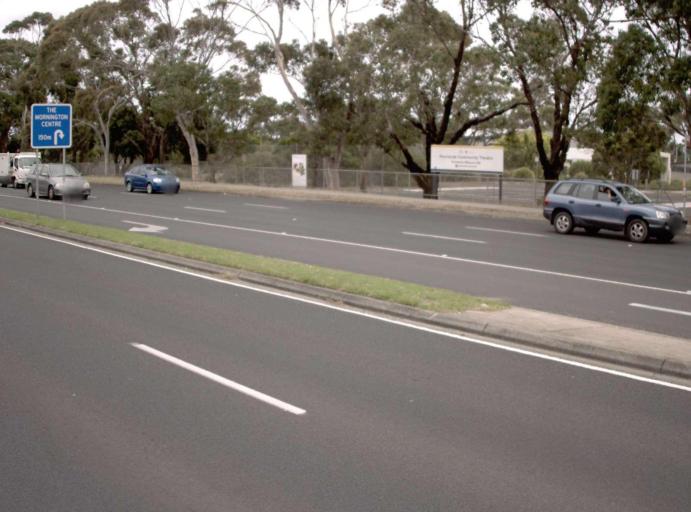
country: AU
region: Victoria
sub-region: Mornington Peninsula
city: Mornington
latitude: -38.2320
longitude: 145.0418
